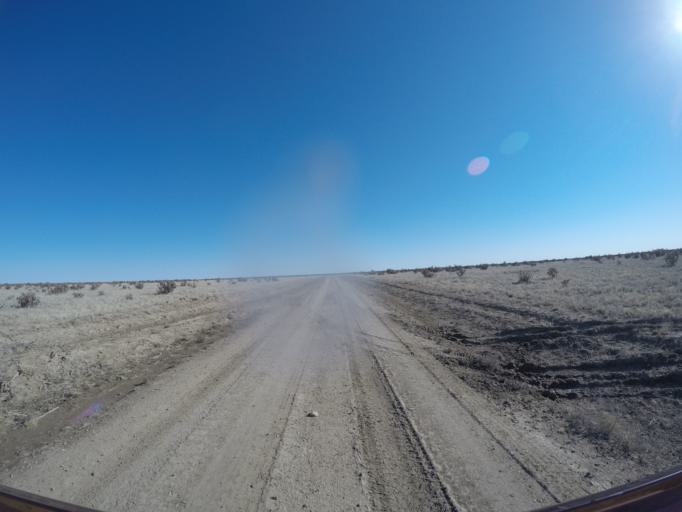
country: US
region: Colorado
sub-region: Otero County
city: La Junta
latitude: 37.6592
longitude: -103.6150
